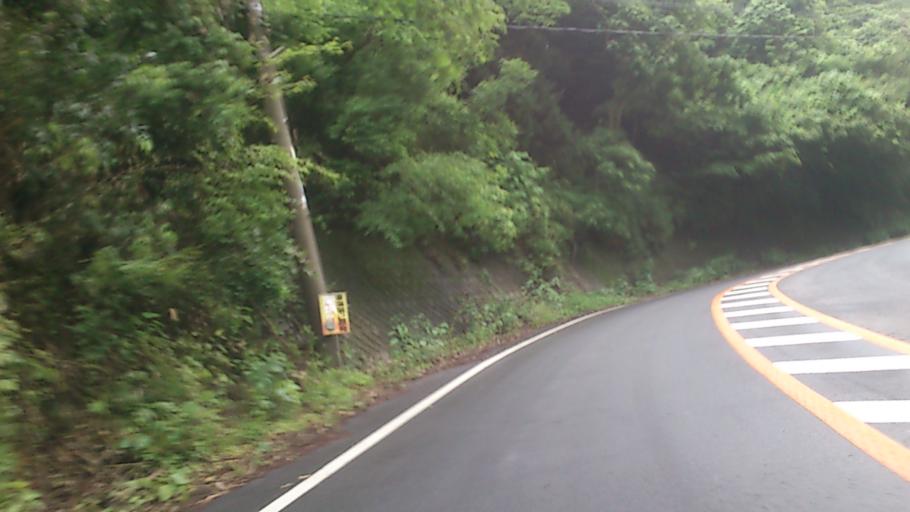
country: JP
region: Ibaraki
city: Omiya
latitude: 36.6285
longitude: 140.3430
